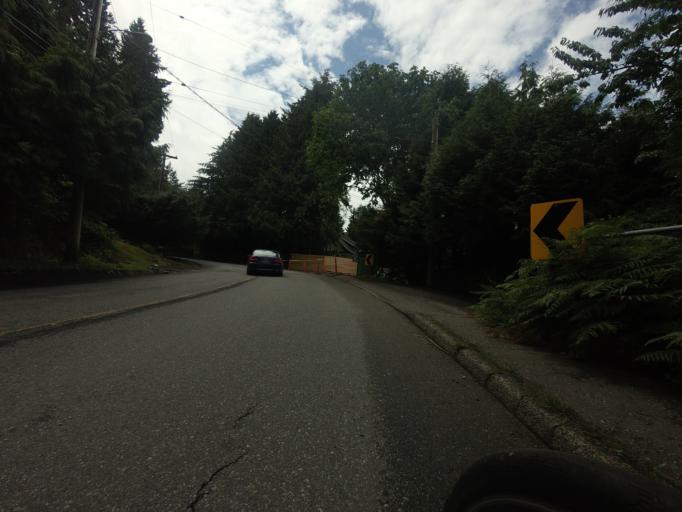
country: CA
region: British Columbia
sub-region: Greater Vancouver Regional District
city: Bowen Island
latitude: 49.3521
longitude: -123.2652
